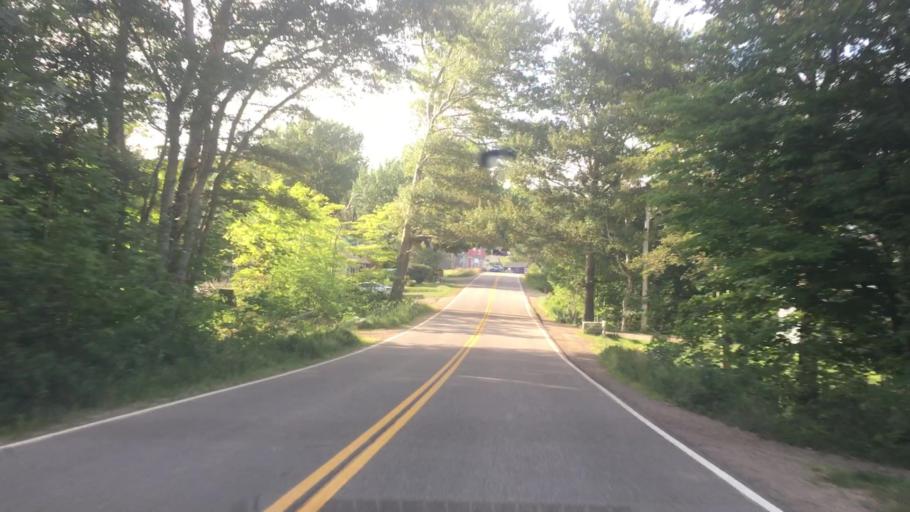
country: CA
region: Nova Scotia
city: Sydney Mines
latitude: 46.8213
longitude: -60.7976
